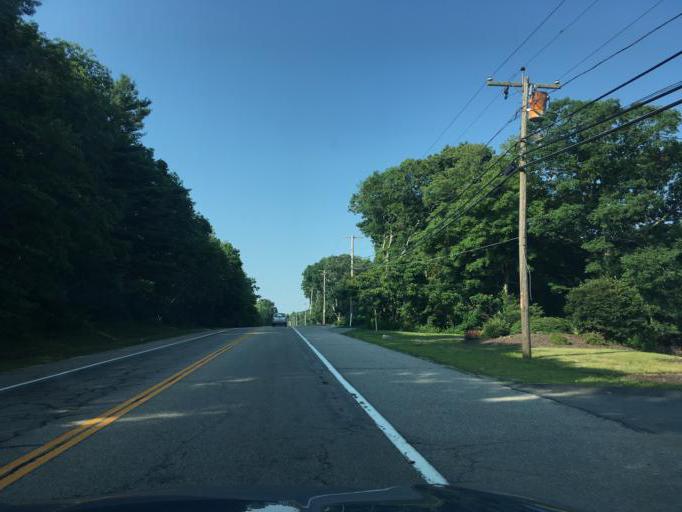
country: US
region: Rhode Island
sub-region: Washington County
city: Exeter
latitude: 41.5303
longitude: -71.5489
